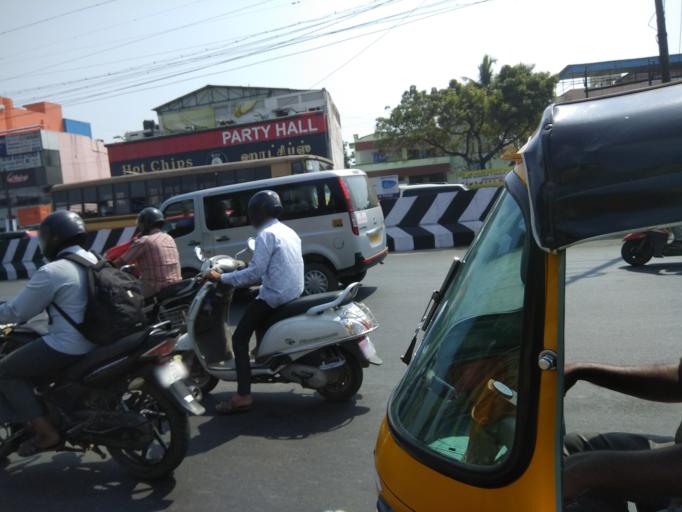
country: IN
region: Tamil Nadu
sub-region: Kancheepuram
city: Pallavaram
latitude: 12.9428
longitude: 80.1333
